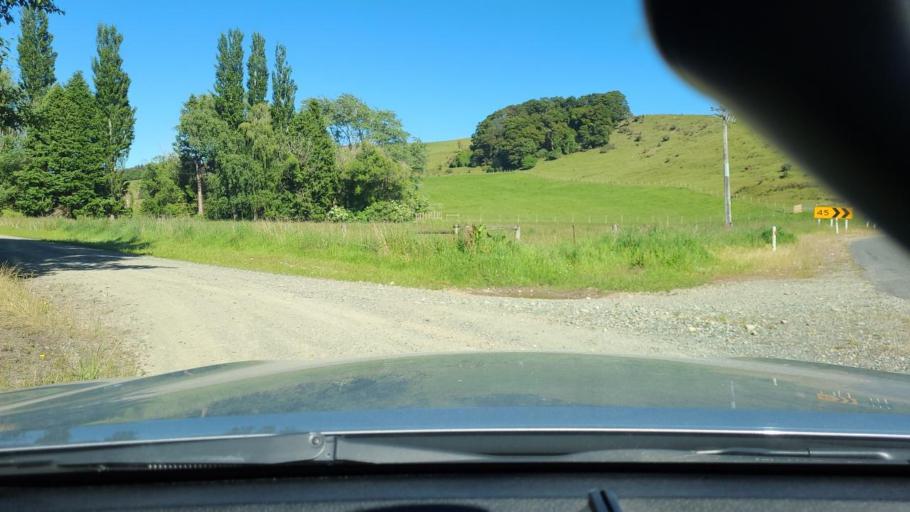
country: NZ
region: Southland
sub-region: Southland District
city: Riverton
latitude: -45.9911
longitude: 167.6302
